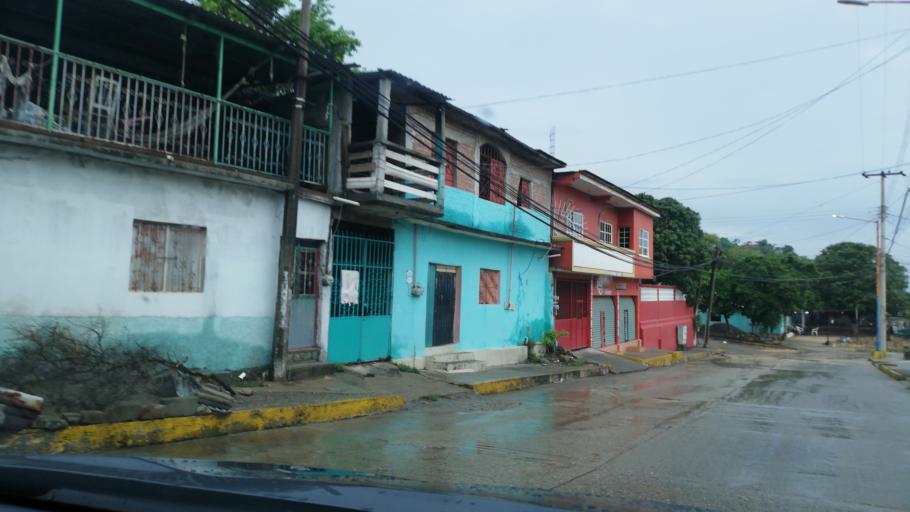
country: MX
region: Oaxaca
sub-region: Salina Cruz
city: Salina Cruz
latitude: 16.1897
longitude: -95.1957
